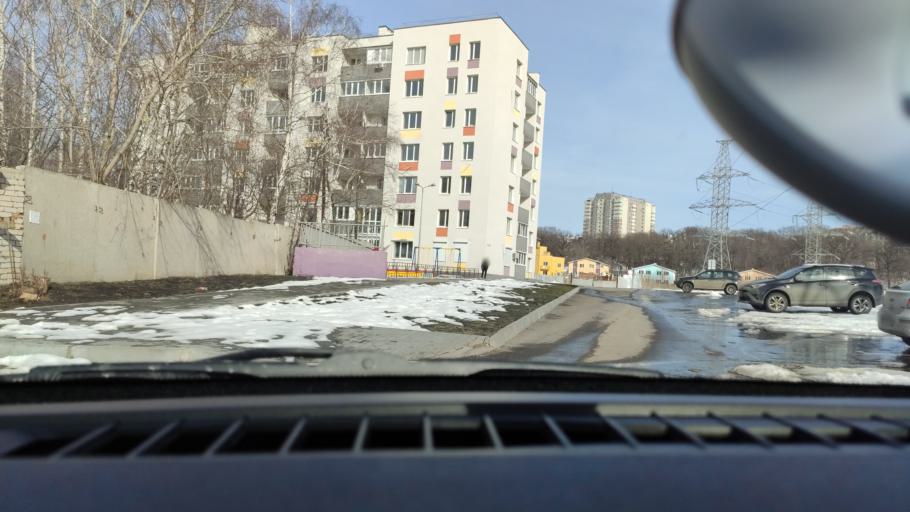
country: RU
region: Samara
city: Samara
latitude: 53.2490
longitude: 50.1910
